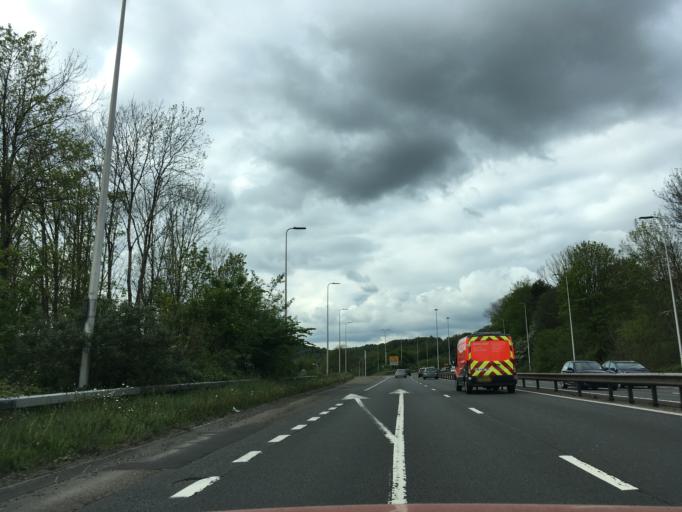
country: GB
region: Wales
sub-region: Rhondda Cynon Taf
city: Pontypridd
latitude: 51.5915
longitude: -3.3217
